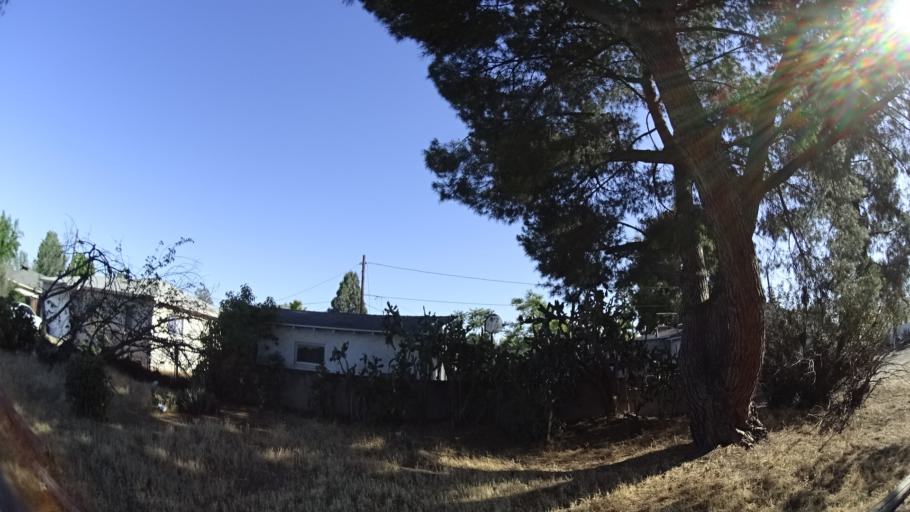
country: US
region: California
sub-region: Los Angeles County
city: North Hollywood
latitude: 34.1812
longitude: -118.3764
